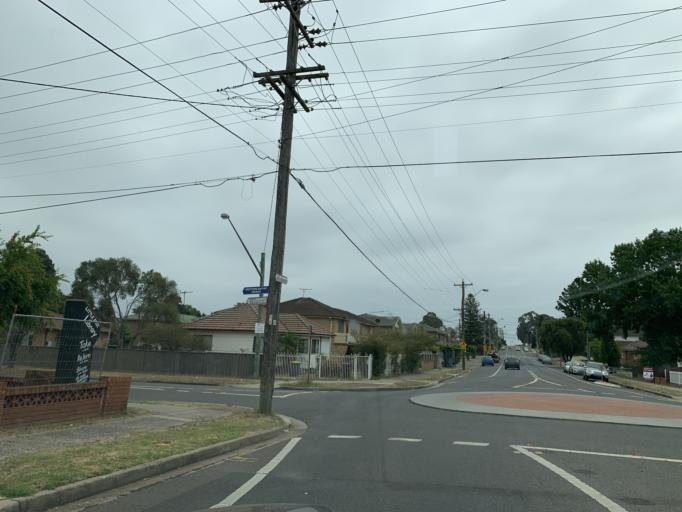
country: AU
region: New South Wales
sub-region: Blacktown
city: Doonside
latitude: -33.7600
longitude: 150.8701
